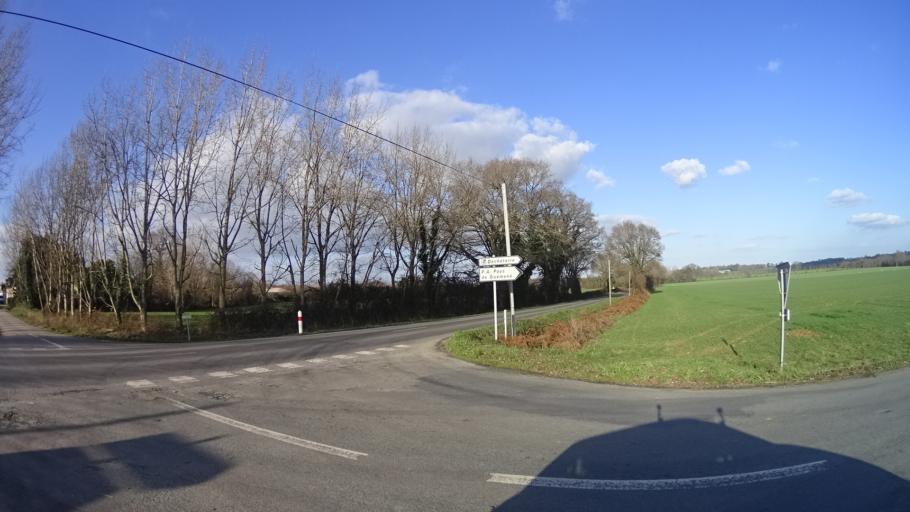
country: FR
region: Pays de la Loire
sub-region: Departement de la Loire-Atlantique
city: Guemene-Penfao
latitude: 47.6373
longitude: -1.8047
